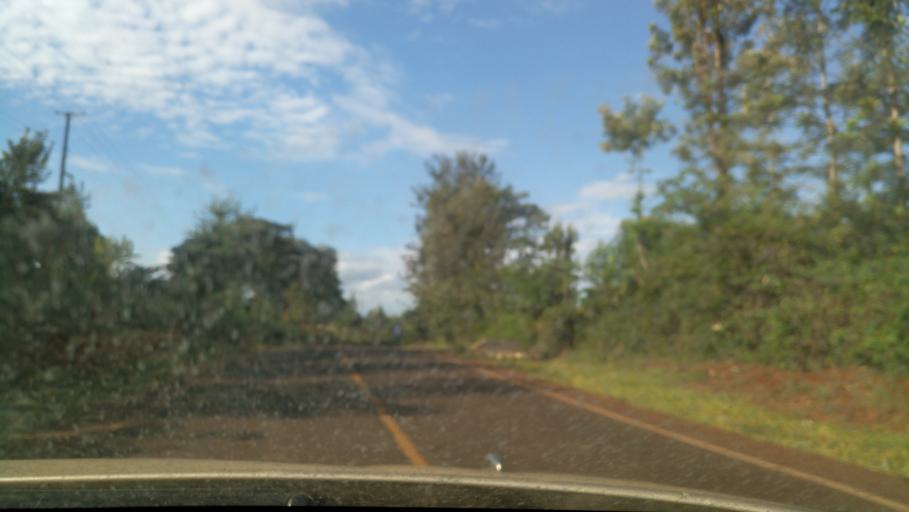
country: KE
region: Murang'a District
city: Maragua
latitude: -0.7885
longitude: 37.0991
